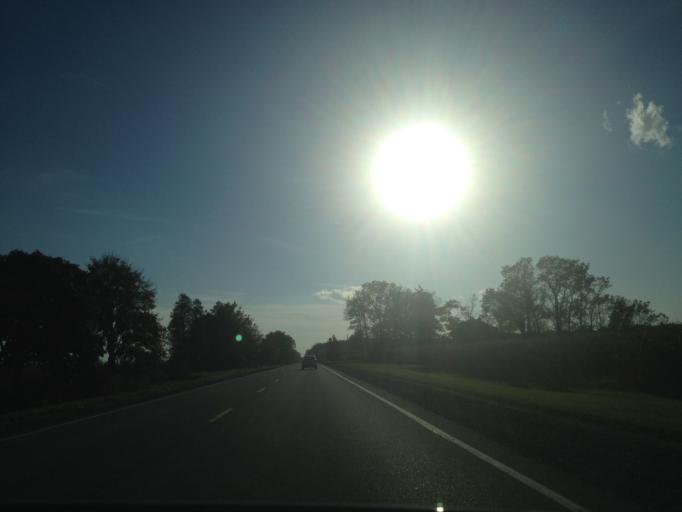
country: CA
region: Ontario
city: Delaware
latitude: 42.5629
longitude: -81.5696
